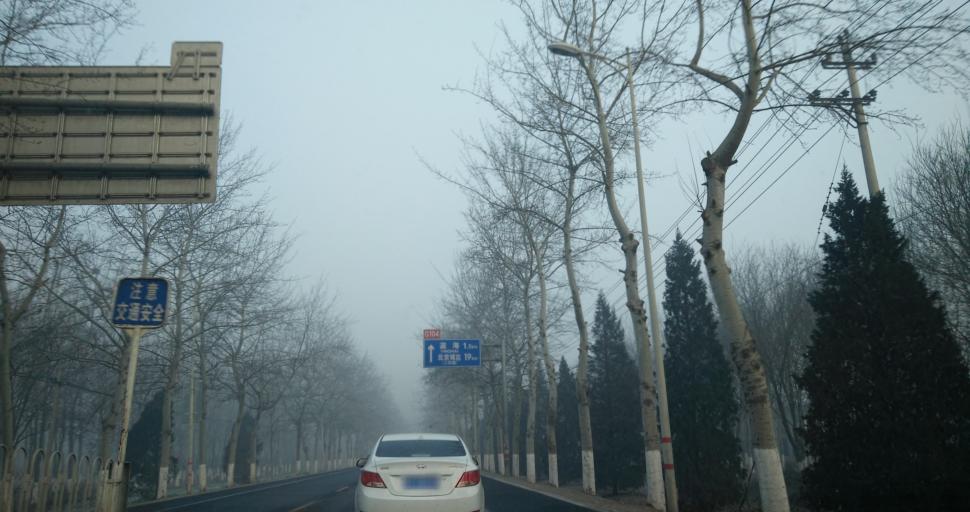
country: CN
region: Beijing
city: Yinghai
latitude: 39.7426
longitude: 116.4487
